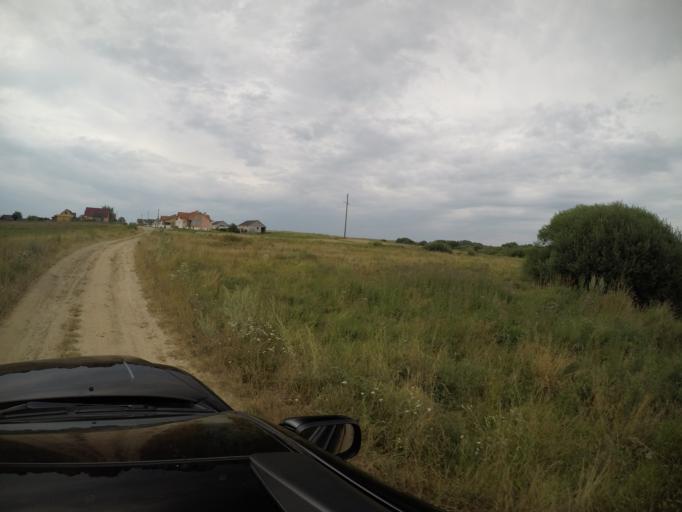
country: BY
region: Grodnenskaya
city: Hal'shany
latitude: 54.2580
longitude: 26.0247
